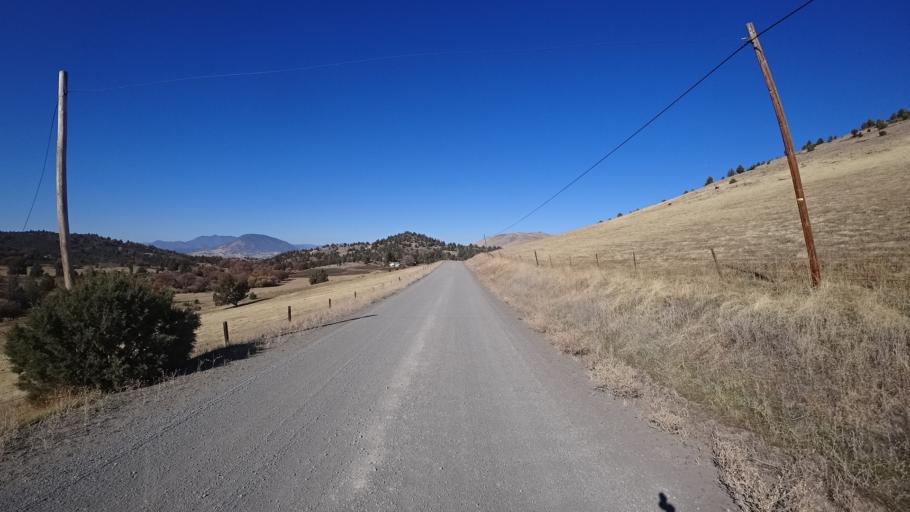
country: US
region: California
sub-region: Siskiyou County
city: Montague
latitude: 41.7975
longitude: -122.3663
